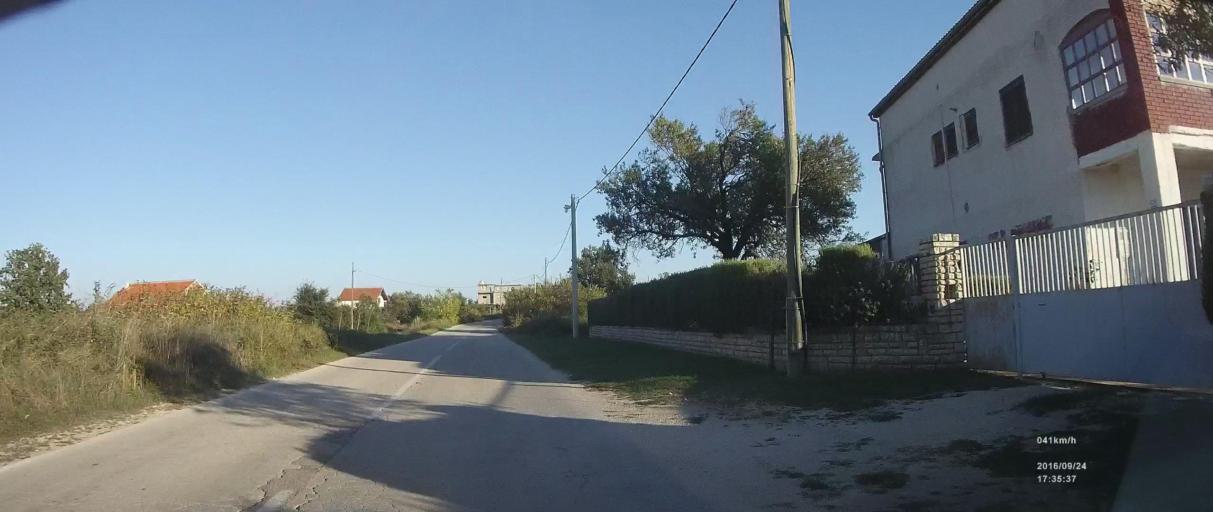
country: HR
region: Zadarska
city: Posedarje
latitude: 44.1596
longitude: 15.4683
